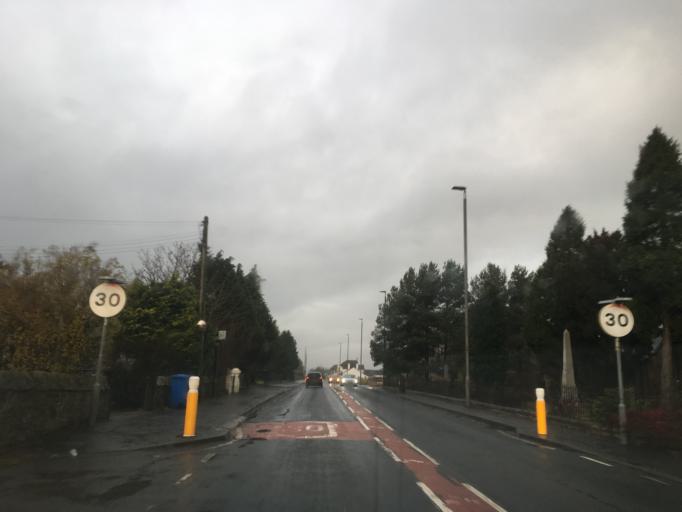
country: GB
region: Scotland
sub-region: Stirling
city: Cowie
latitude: 56.1002
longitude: -3.8604
